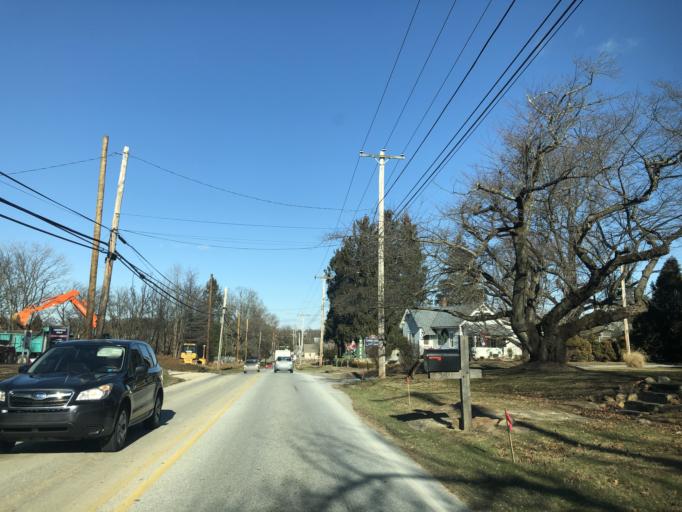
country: US
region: Pennsylvania
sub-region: Chester County
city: Kennett Square
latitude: 39.8704
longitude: -75.7174
